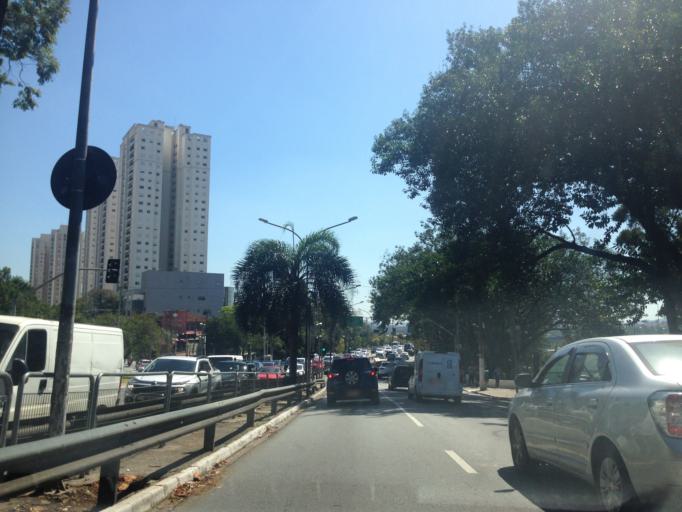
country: BR
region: Sao Paulo
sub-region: Osasco
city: Osasco
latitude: -23.5198
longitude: -46.7226
